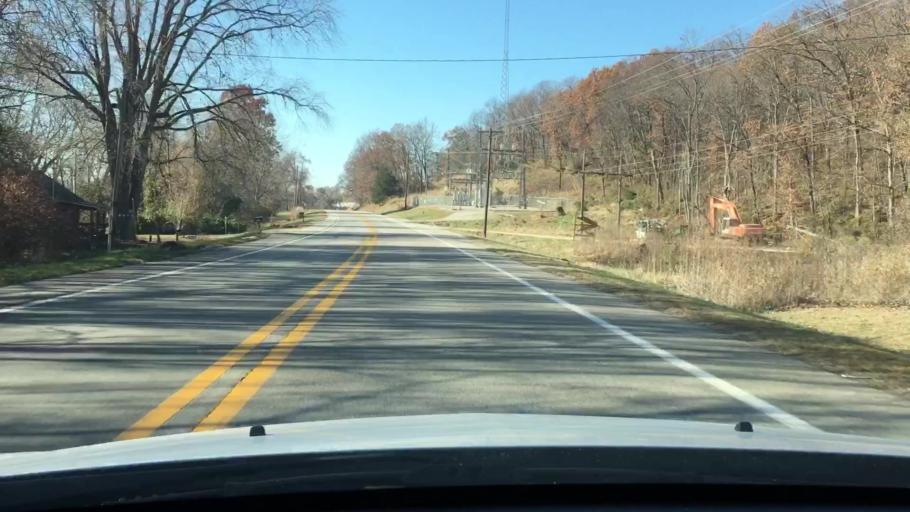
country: US
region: Missouri
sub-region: Pike County
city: Louisiana
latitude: 39.5151
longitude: -90.9638
